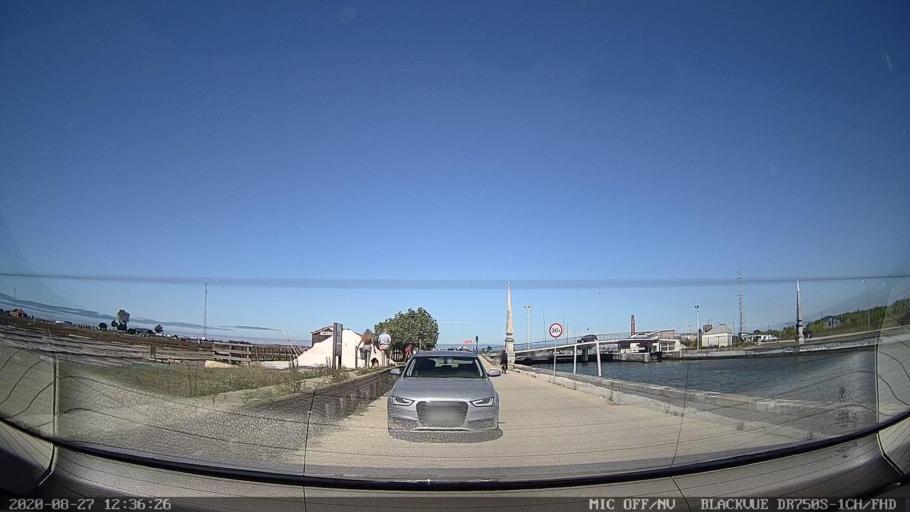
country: PT
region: Aveiro
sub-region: Aveiro
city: Aveiro
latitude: 40.6449
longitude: -8.6617
